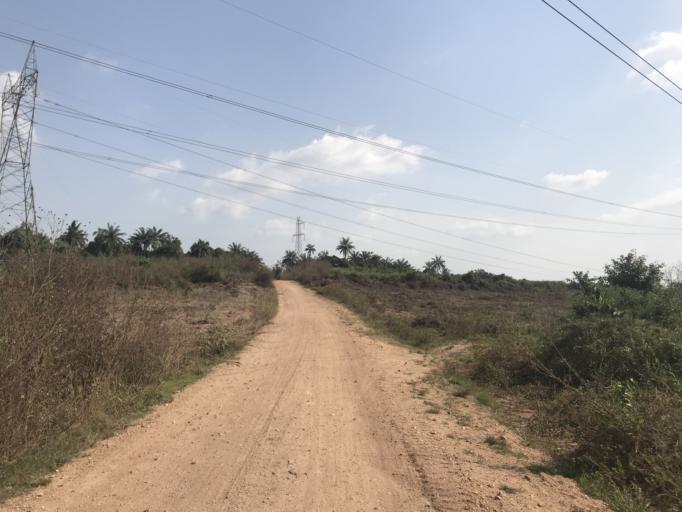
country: NG
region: Osun
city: Ikirun
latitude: 7.8695
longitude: 4.5854
